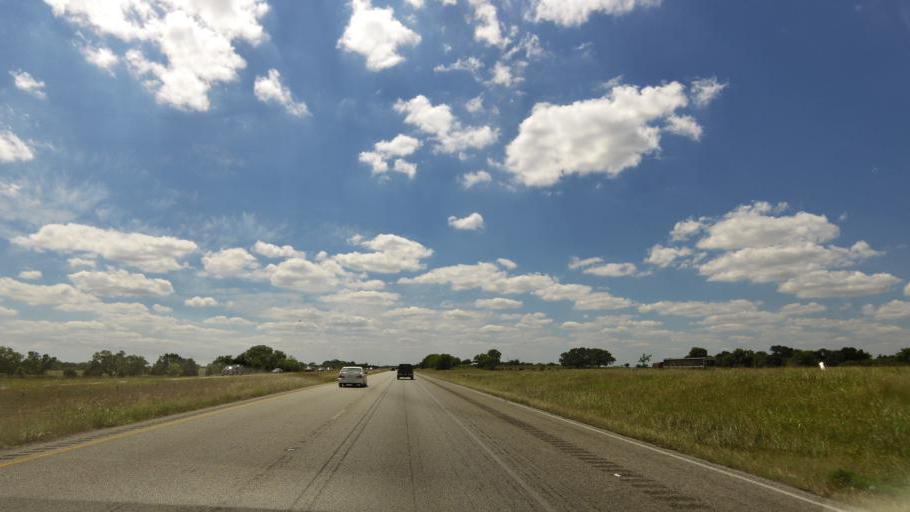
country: US
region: Texas
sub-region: Fayette County
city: Schulenburg
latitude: 29.6901
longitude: -96.9680
